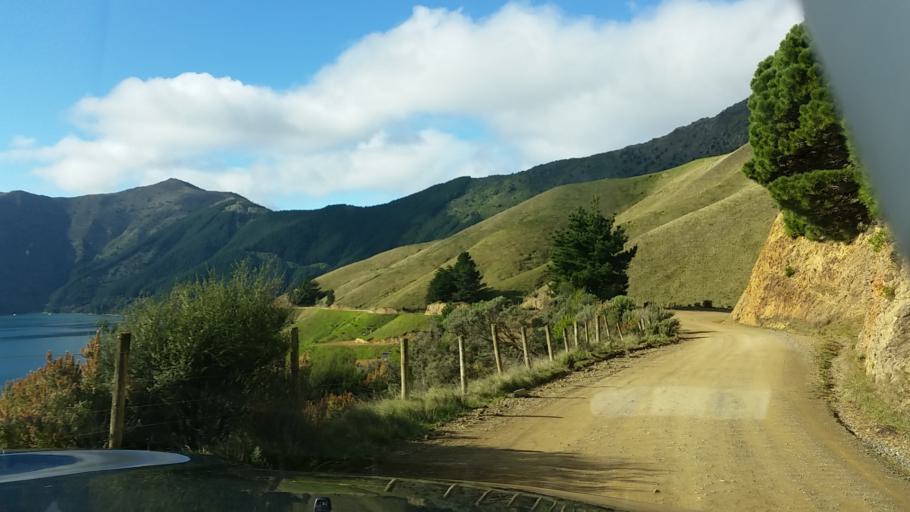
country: NZ
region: Marlborough
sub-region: Marlborough District
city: Picton
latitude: -40.9845
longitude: 173.8335
